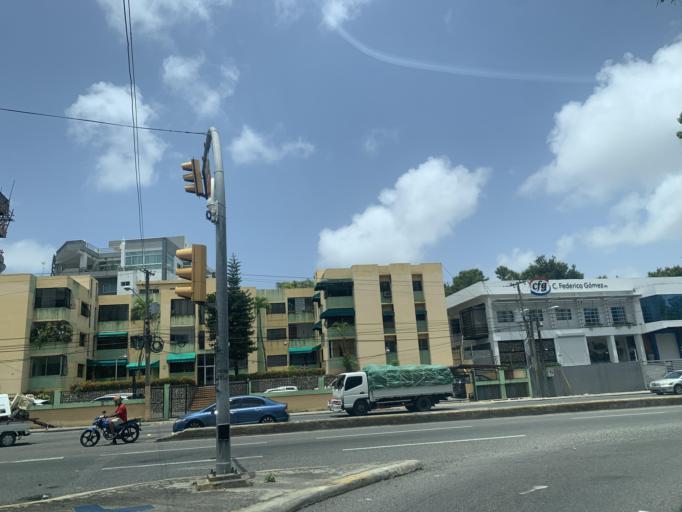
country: DO
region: Nacional
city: La Agustina
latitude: 18.4896
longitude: -69.9471
